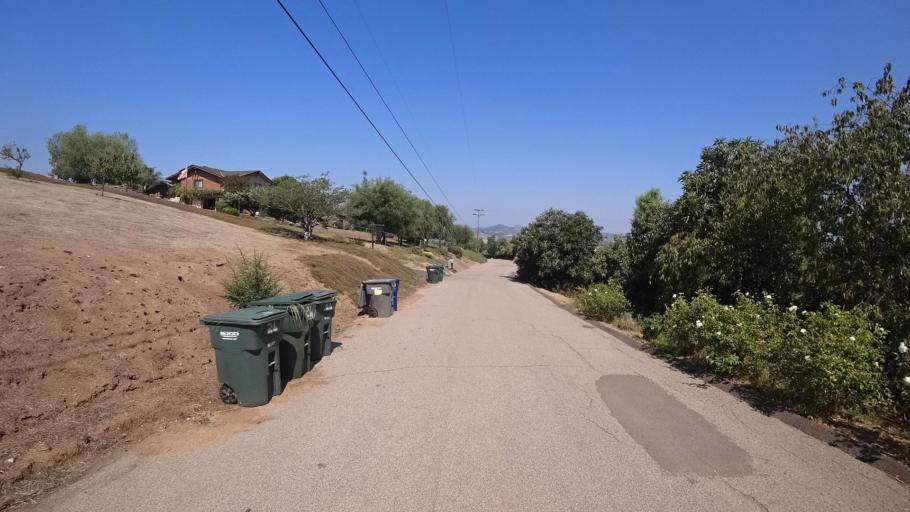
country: US
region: California
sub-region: San Diego County
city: Bonsall
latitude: 33.2467
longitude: -117.2368
